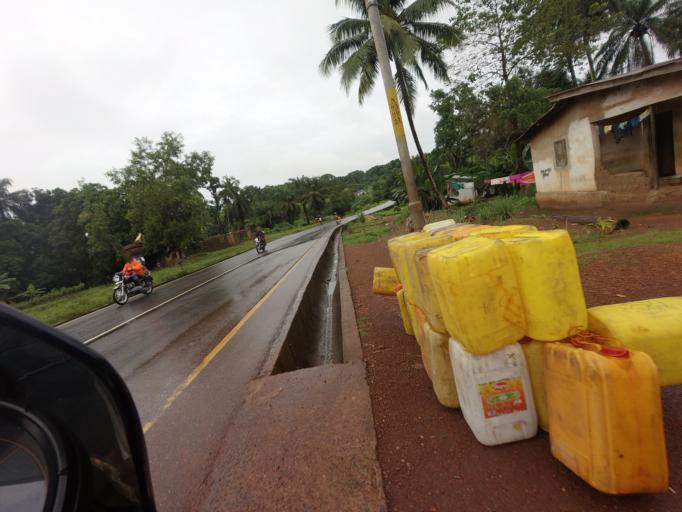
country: SL
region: Northern Province
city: Kambia
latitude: 9.1197
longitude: -12.9193
